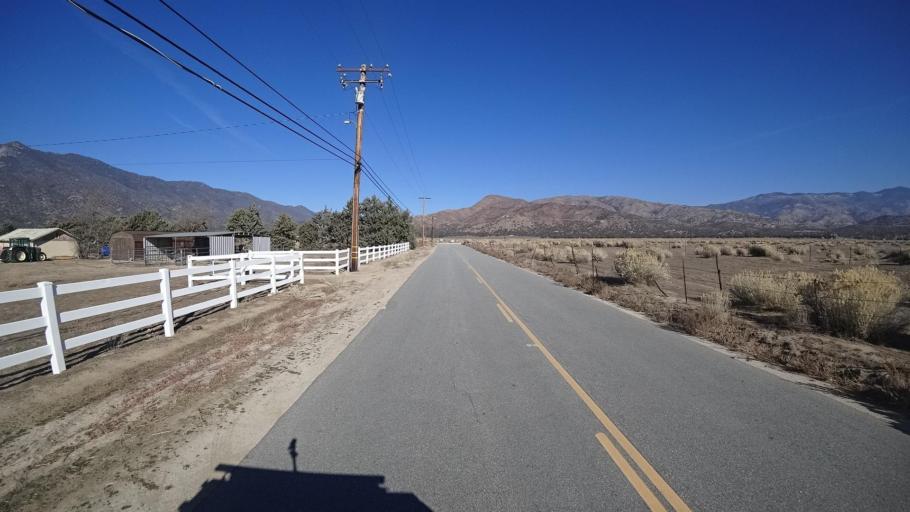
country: US
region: California
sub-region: Kern County
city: Bodfish
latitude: 35.4115
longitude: -118.5236
